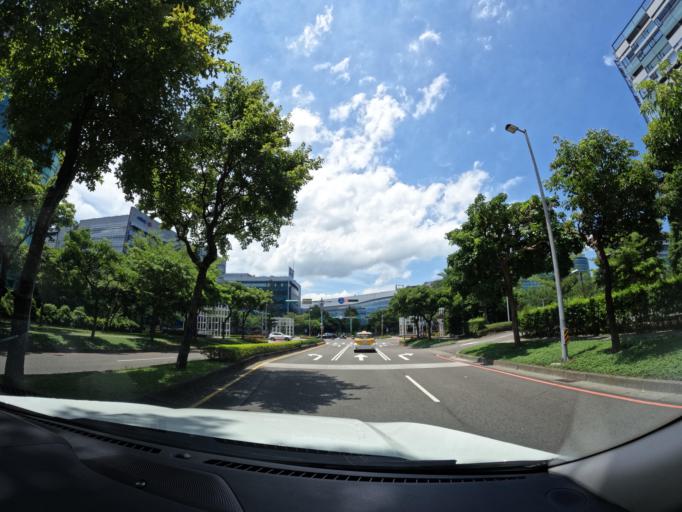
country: TW
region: Taiwan
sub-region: Taoyuan
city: Taoyuan
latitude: 25.0488
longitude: 121.3761
